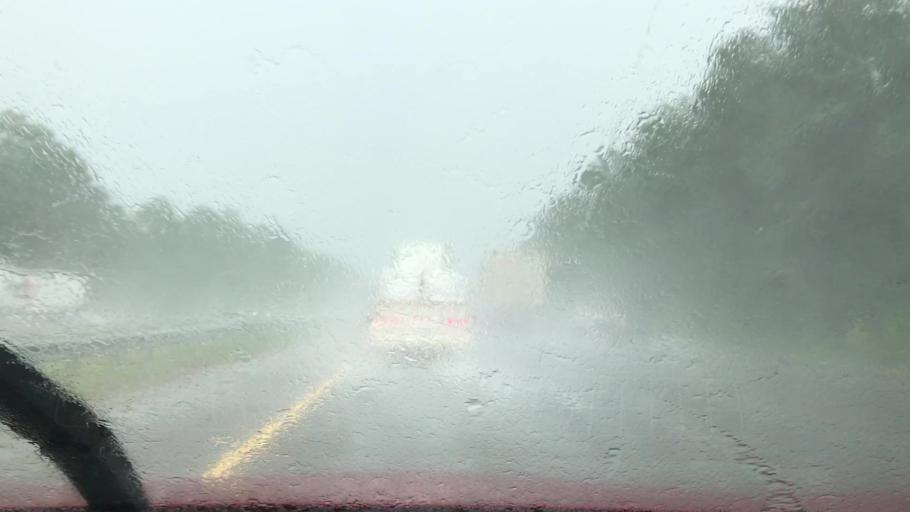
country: US
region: South Carolina
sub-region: Berkeley County
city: Ladson
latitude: 33.0048
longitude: -80.1020
